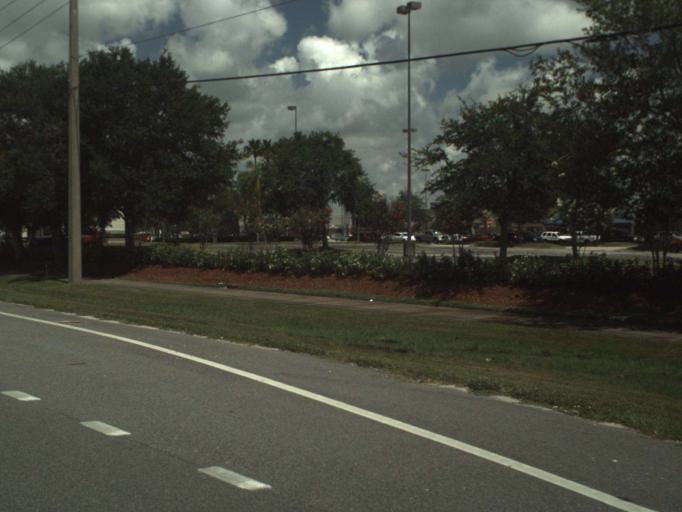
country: US
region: Florida
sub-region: Indian River County
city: West Vero Corridor
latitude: 27.6391
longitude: -80.4512
